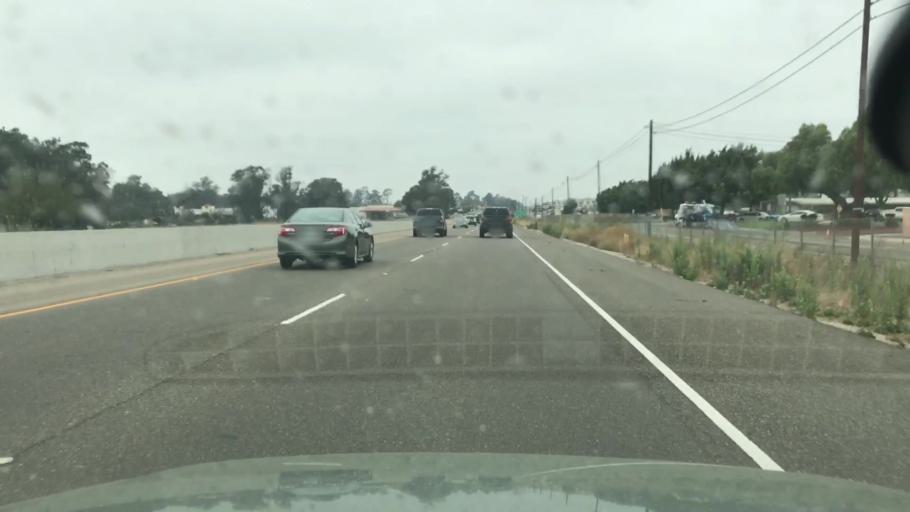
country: US
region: California
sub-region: Santa Barbara County
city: Orcutt
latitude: 34.8902
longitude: -120.4364
